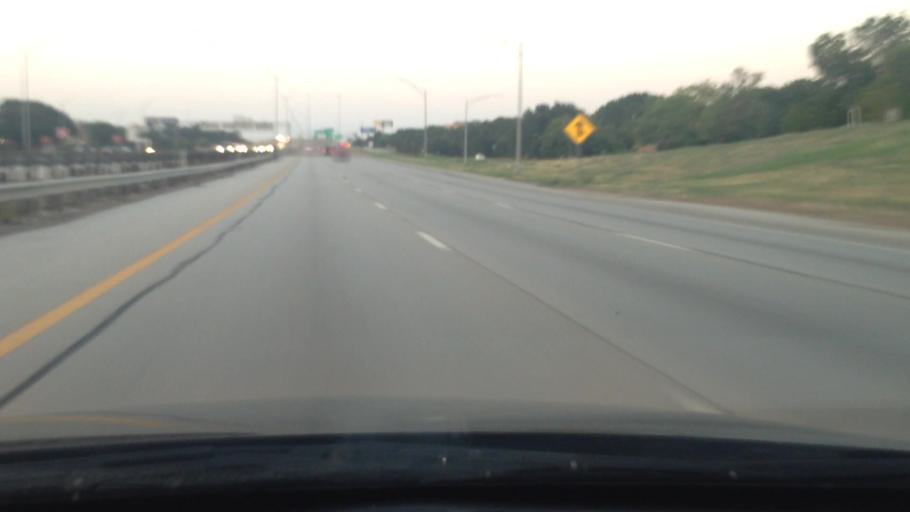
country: US
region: Texas
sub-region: Tarrant County
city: Richland Hills
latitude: 32.7463
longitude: -97.2221
